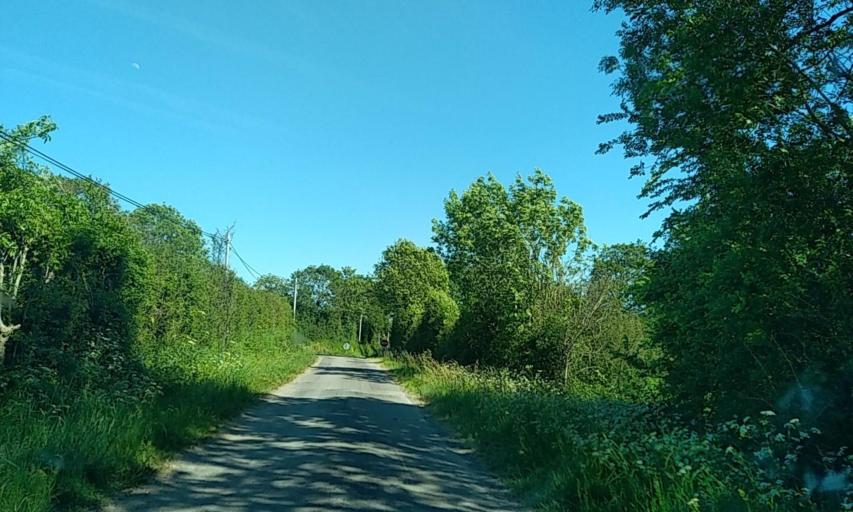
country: FR
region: Poitou-Charentes
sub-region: Departement des Deux-Sevres
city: Boisme
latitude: 46.7875
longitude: -0.4527
